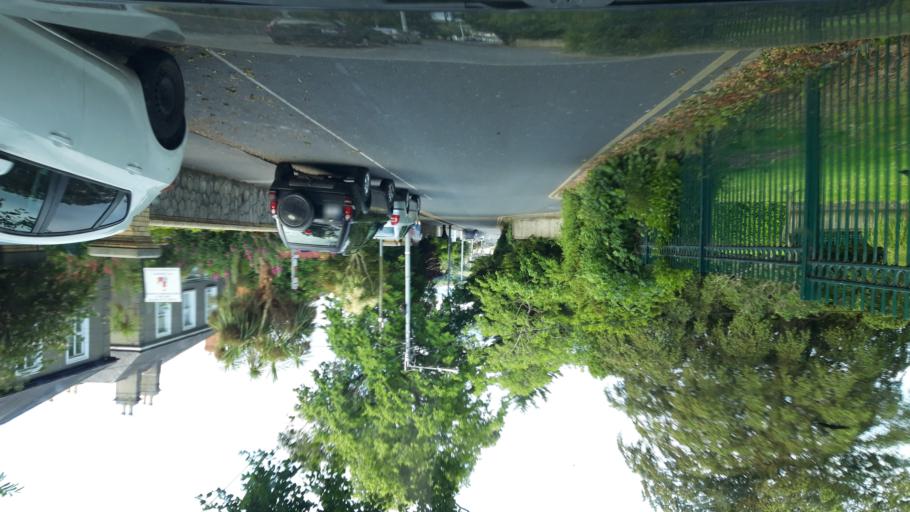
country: IE
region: Leinster
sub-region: Wicklow
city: Bray
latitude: 53.2005
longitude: -6.1022
